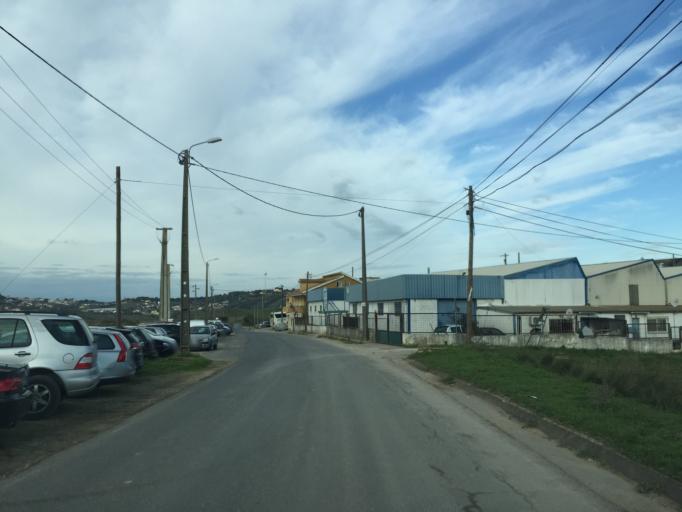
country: PT
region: Lisbon
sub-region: Odivelas
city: Canecas
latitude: 38.8258
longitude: -9.2449
